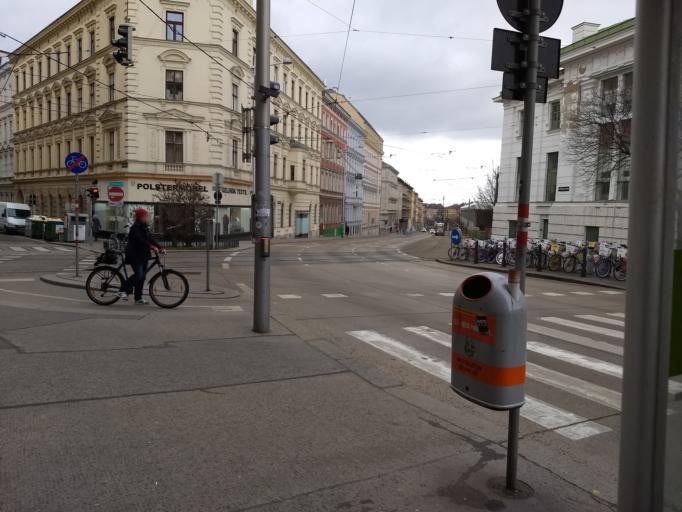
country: AT
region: Vienna
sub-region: Wien Stadt
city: Vienna
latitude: 48.2219
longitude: 16.3431
